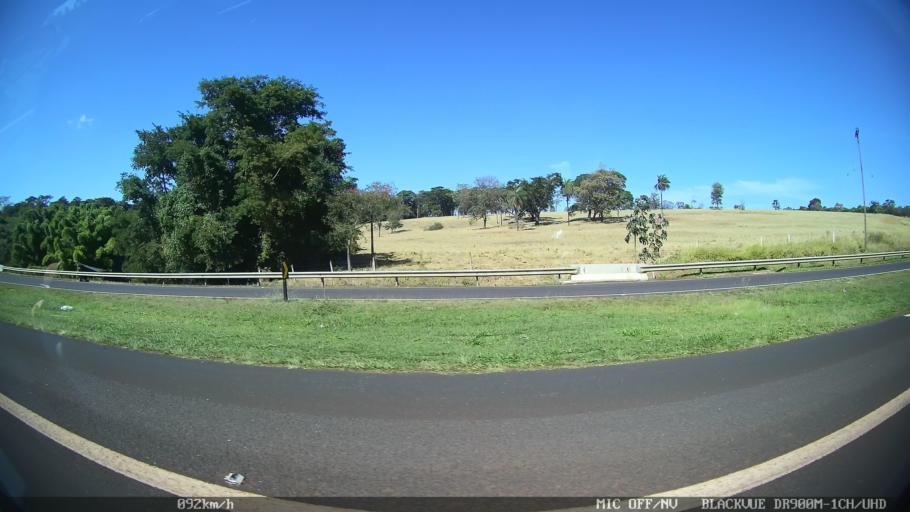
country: BR
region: Sao Paulo
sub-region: Franca
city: Franca
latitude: -20.5634
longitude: -47.4166
